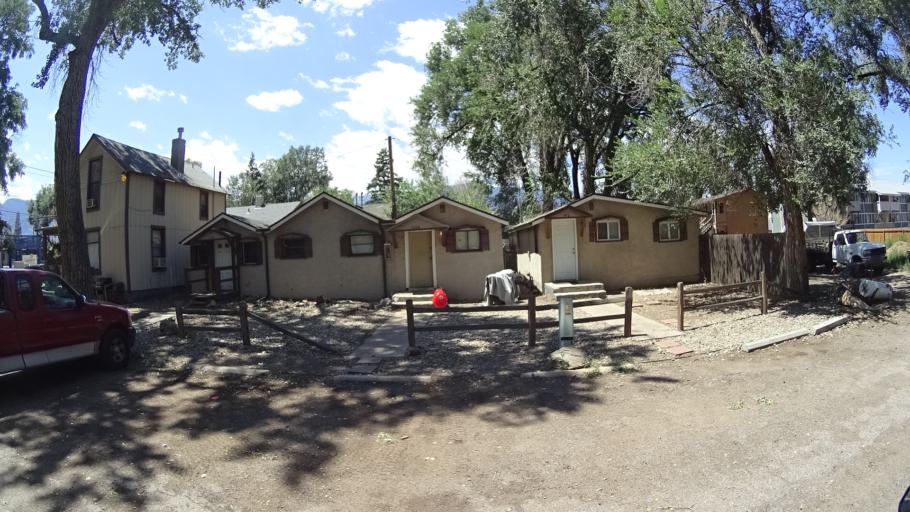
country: US
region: Colorado
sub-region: El Paso County
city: Colorado Springs
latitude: 38.8131
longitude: -104.8208
